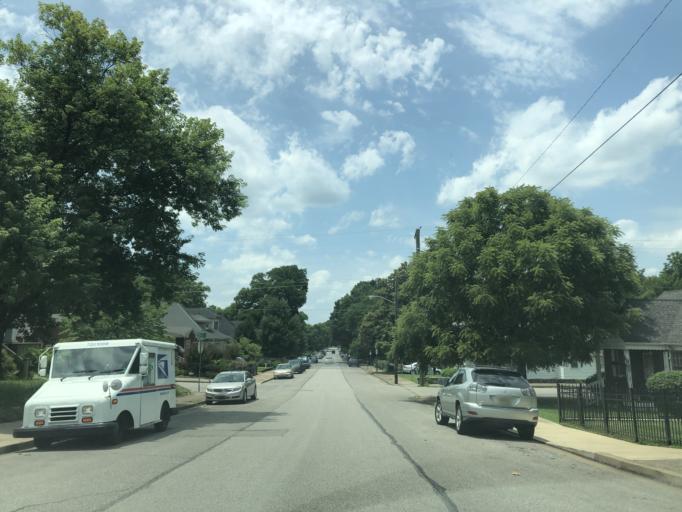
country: US
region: Tennessee
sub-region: Davidson County
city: Nashville
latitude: 36.1848
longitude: -86.7495
